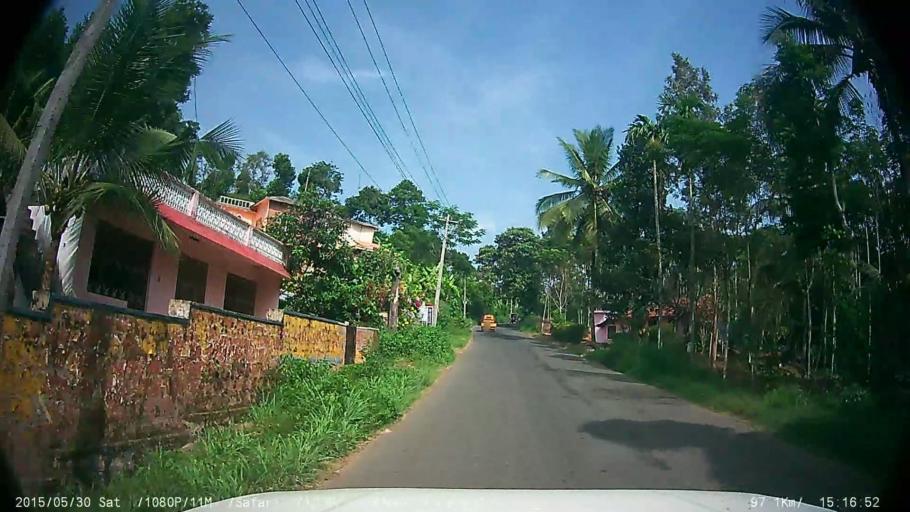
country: IN
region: Kerala
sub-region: Wayanad
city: Panamaram
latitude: 11.7754
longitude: 76.0584
